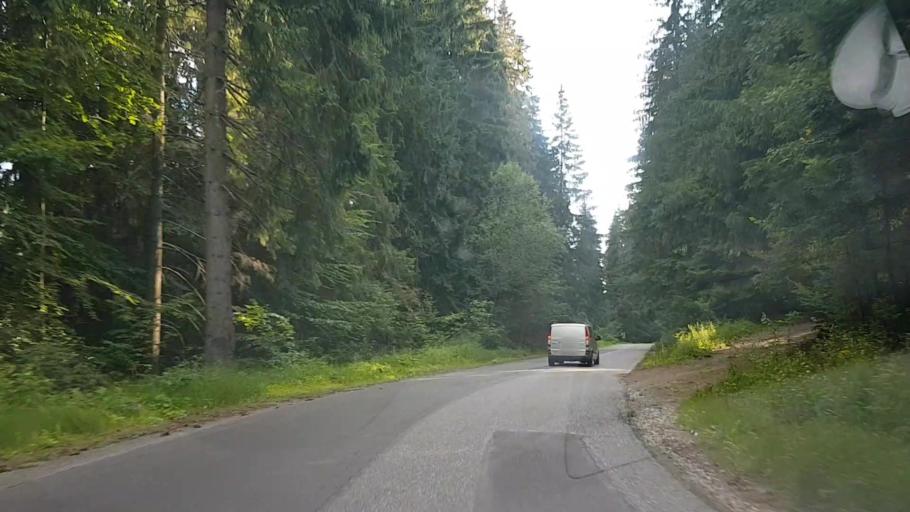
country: RO
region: Harghita
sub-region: Comuna Remetea
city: Remetea
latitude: 46.6727
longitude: 25.3575
